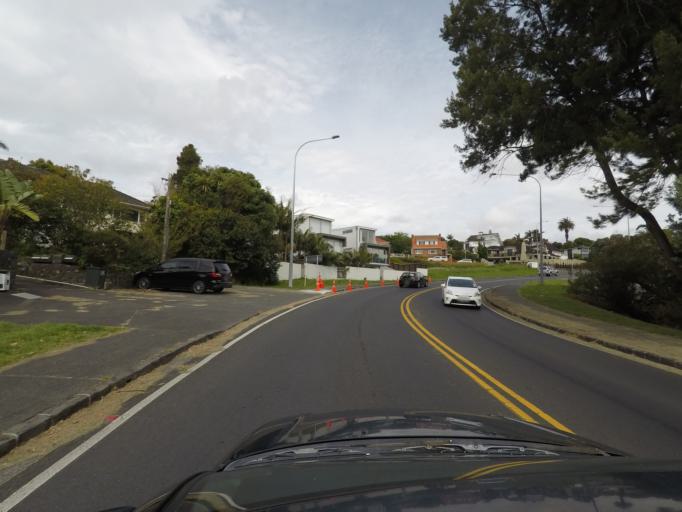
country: NZ
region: Auckland
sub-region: Auckland
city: Auckland
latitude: -36.8558
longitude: 174.8099
